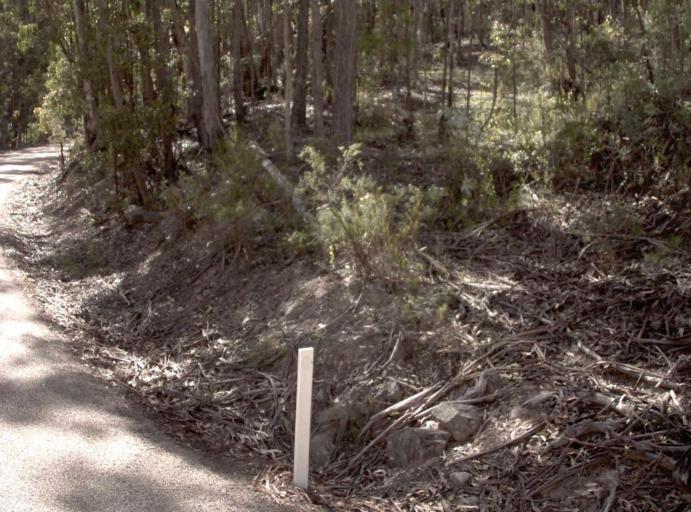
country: AU
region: Victoria
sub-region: East Gippsland
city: Lakes Entrance
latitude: -37.4071
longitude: 148.1229
